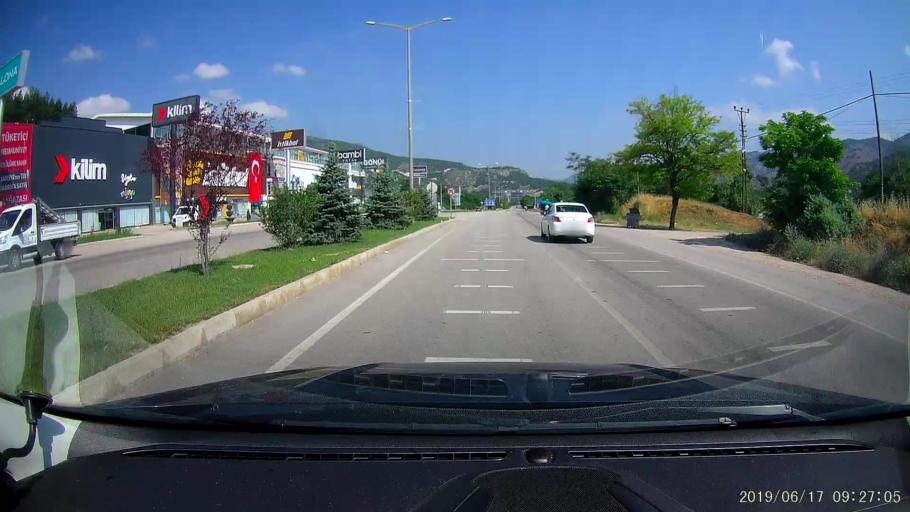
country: TR
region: Amasya
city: Amasya
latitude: 40.6737
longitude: 35.8293
